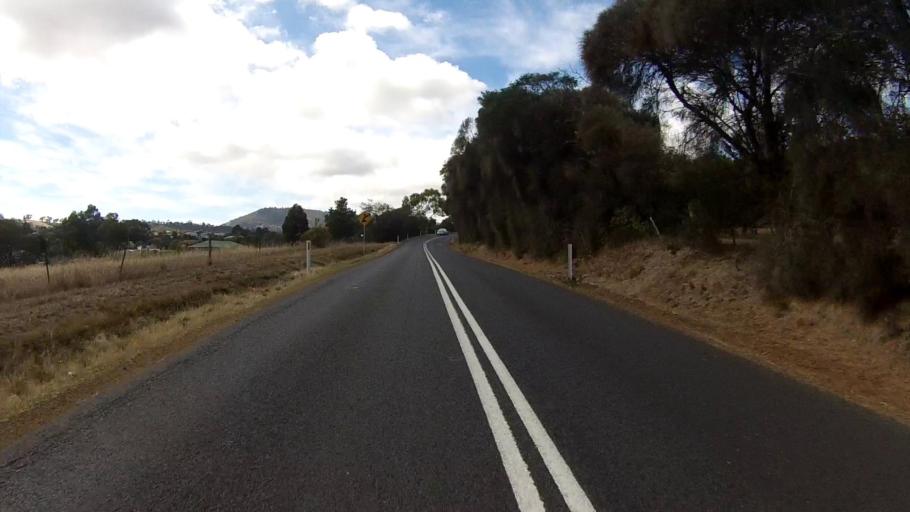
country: AU
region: Tasmania
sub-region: Glenorchy
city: Austins Ferry
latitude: -42.7274
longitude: 147.2870
